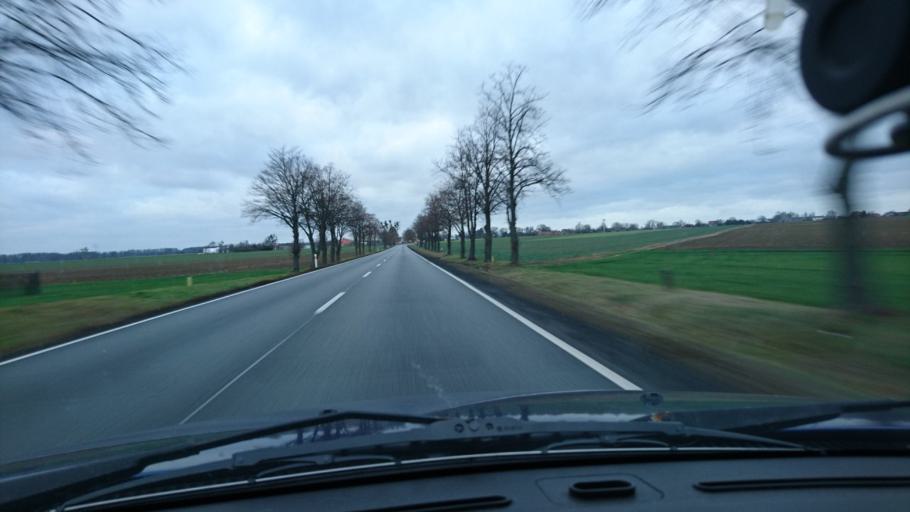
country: PL
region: Opole Voivodeship
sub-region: Powiat kluczborski
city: Kluczbork
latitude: 51.0201
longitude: 18.1965
